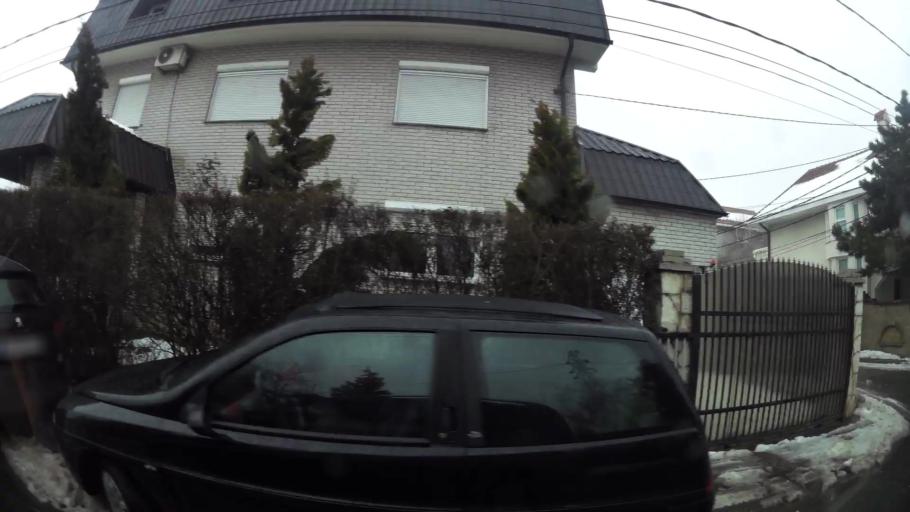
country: RS
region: Central Serbia
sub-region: Belgrade
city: Zvezdara
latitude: 44.7803
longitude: 20.5193
